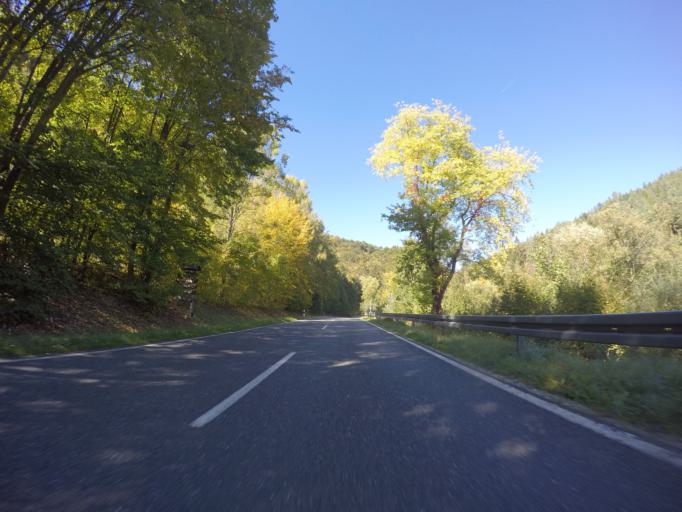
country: DE
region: Bavaria
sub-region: Upper Franconia
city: Gossweinstein
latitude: 49.7829
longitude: 11.3328
